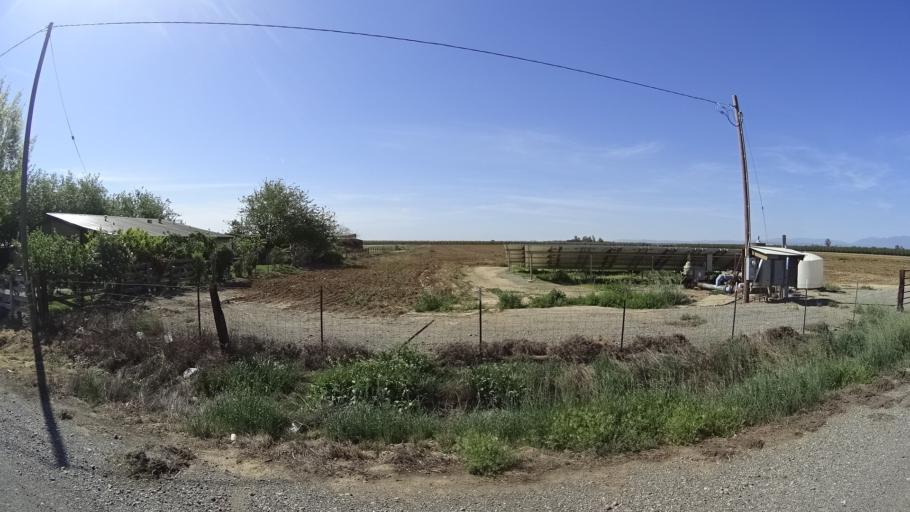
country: US
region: California
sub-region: Glenn County
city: Willows
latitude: 39.6240
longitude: -122.1810
